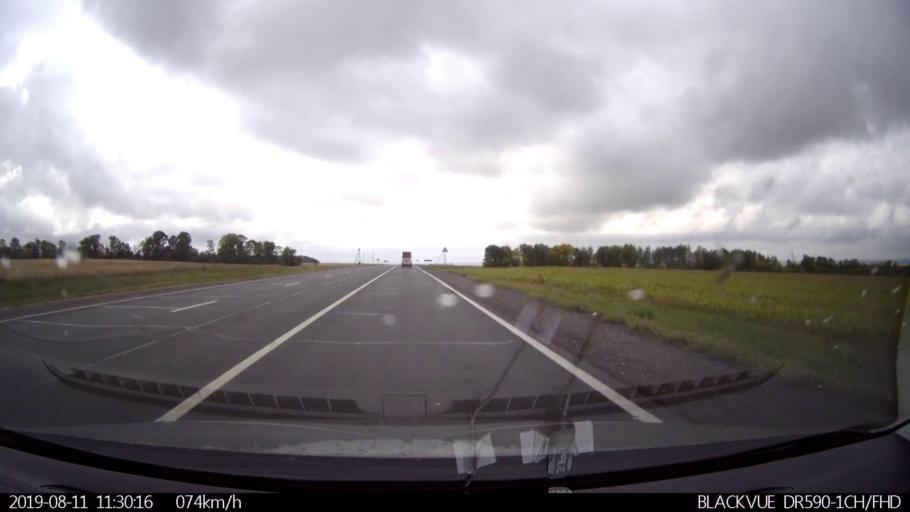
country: RU
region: Ulyanovsk
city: Krasnyy Gulyay
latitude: 54.0607
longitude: 48.2200
